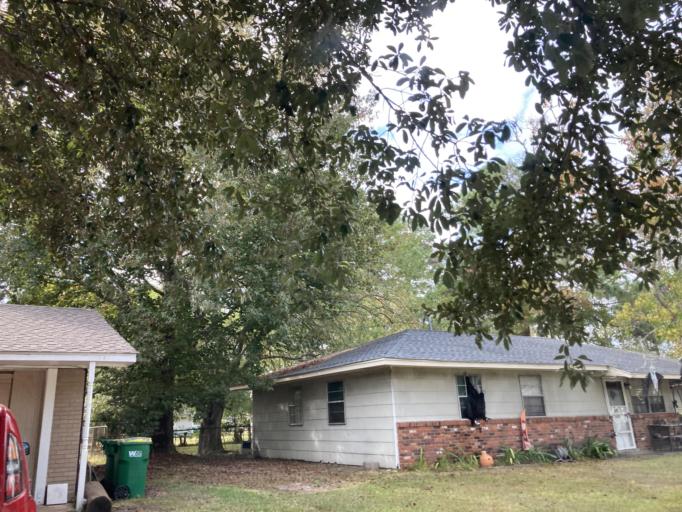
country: US
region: Mississippi
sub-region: Jackson County
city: Gulf Hills
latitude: 30.4364
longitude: -88.8235
